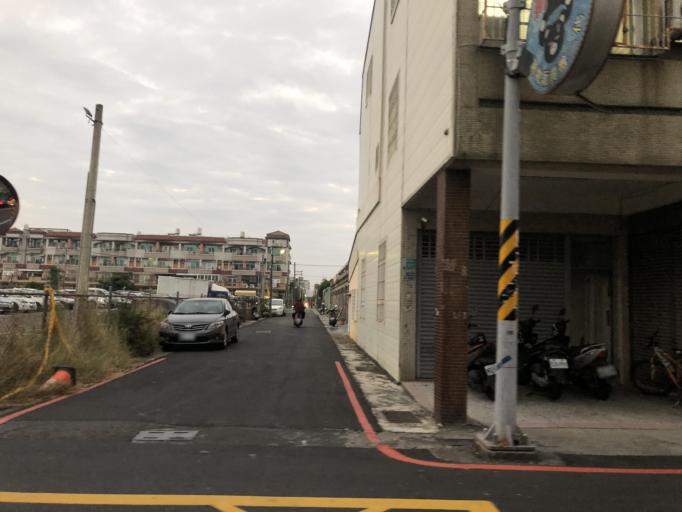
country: TW
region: Taiwan
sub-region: Tainan
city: Tainan
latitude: 23.0206
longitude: 120.2640
